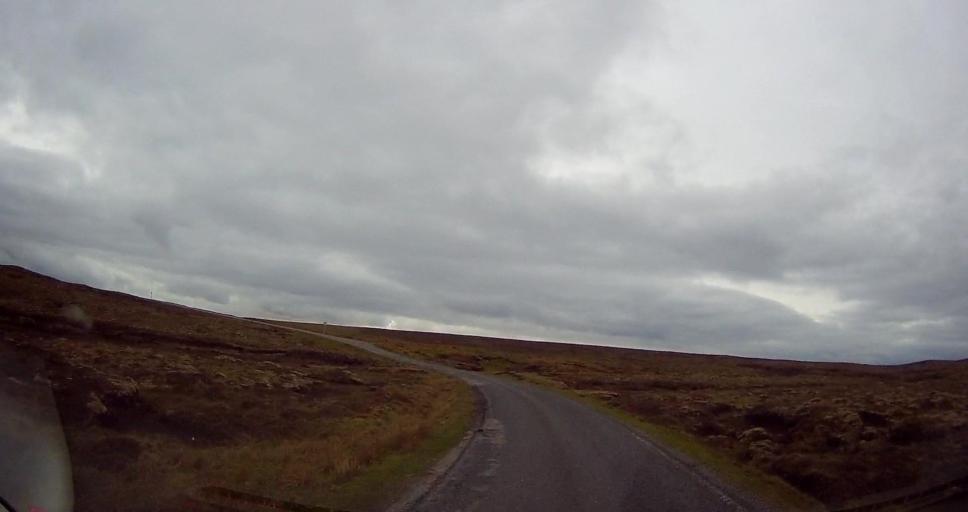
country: GB
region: Scotland
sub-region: Shetland Islands
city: Shetland
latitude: 60.5096
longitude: -1.1379
